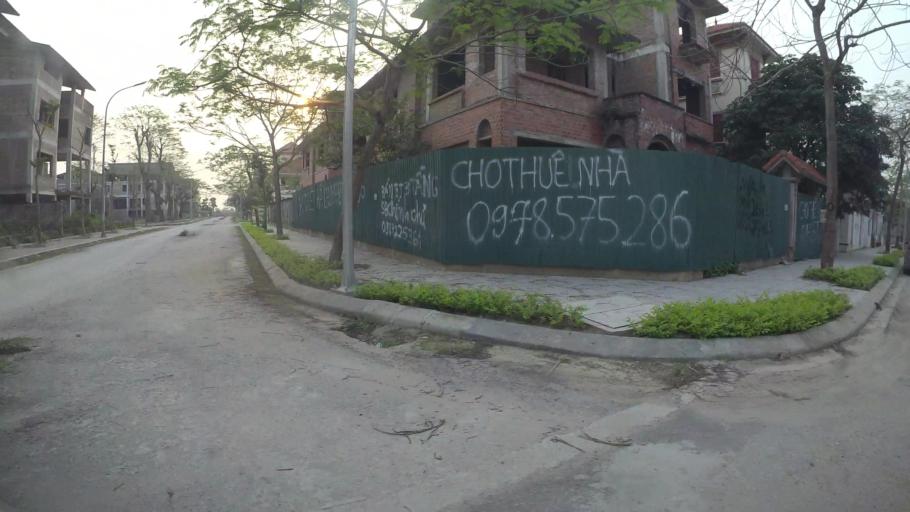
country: VN
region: Ha Noi
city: Cau Dien
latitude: 21.0003
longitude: 105.7295
